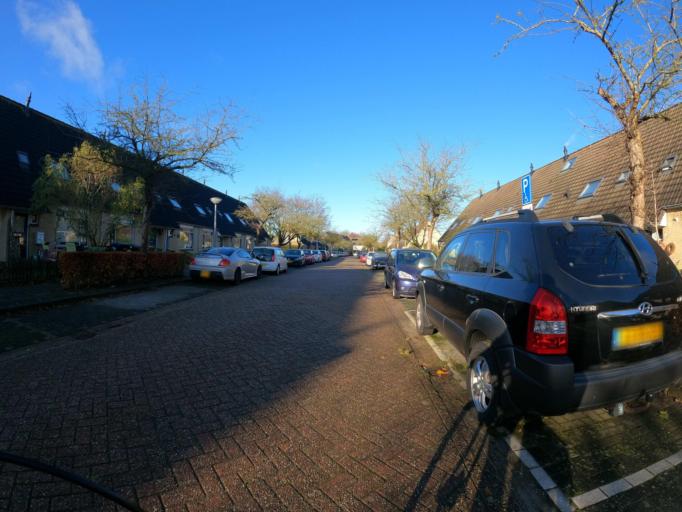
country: NL
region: Flevoland
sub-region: Gemeente Zeewolde
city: Zeewolde
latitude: 52.3214
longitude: 5.5370
